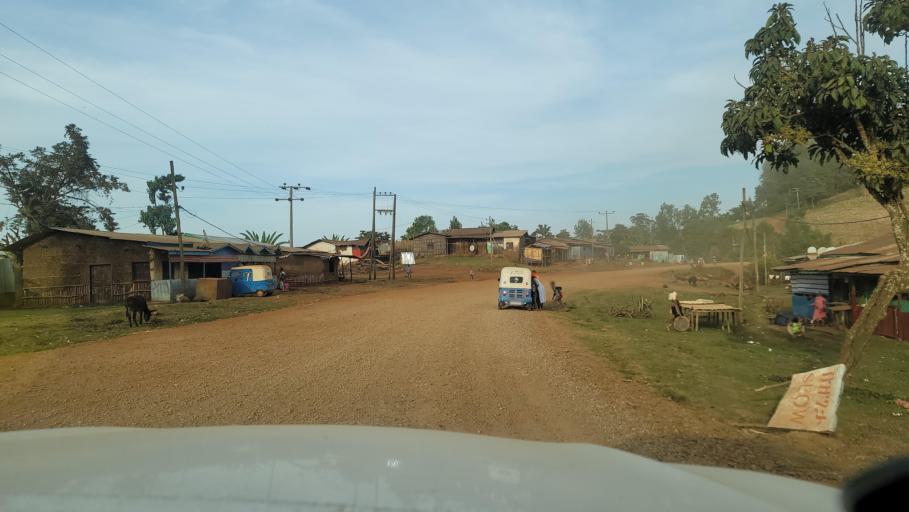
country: ET
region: Oromiya
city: Agaro
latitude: 7.8171
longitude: 36.5184
